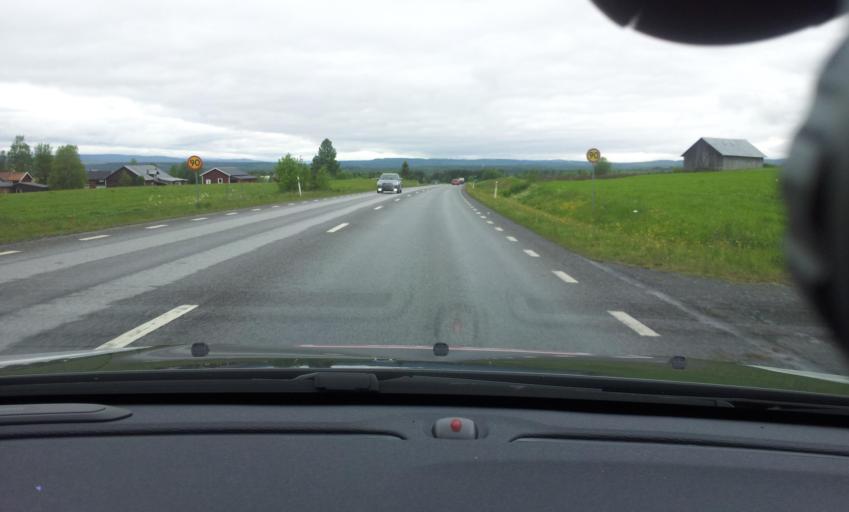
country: SE
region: Jaemtland
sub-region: Krokoms Kommun
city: Valla
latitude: 63.3043
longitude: 13.8855
